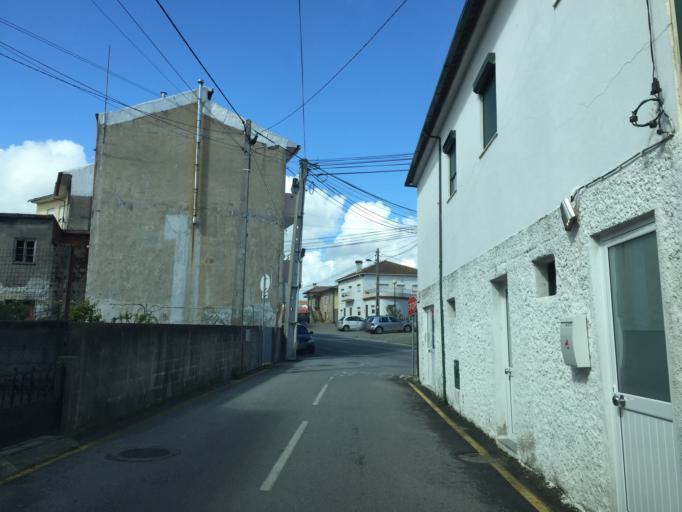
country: PT
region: Viseu
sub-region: Viseu
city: Abraveses
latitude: 40.6633
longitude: -7.9382
